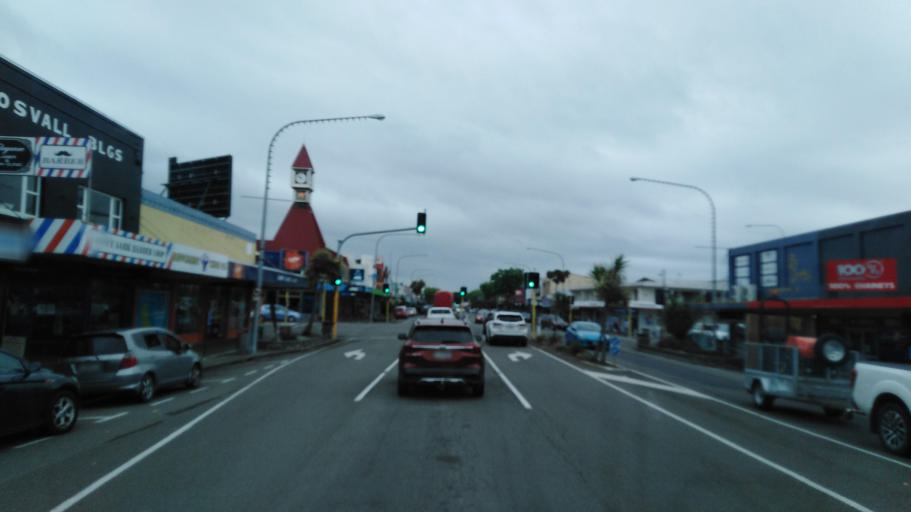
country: NZ
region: Manawatu-Wanganui
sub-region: Horowhenua District
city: Levin
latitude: -40.6215
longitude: 175.2871
